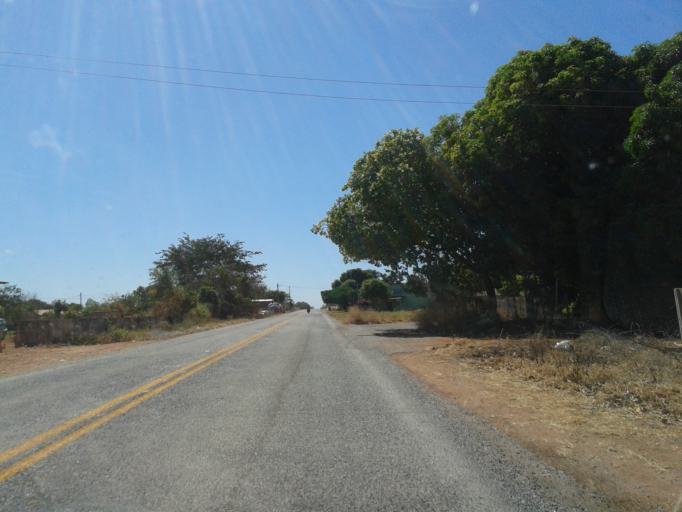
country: BR
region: Goias
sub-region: Sao Miguel Do Araguaia
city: Sao Miguel do Araguaia
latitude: -13.2632
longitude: -50.1481
